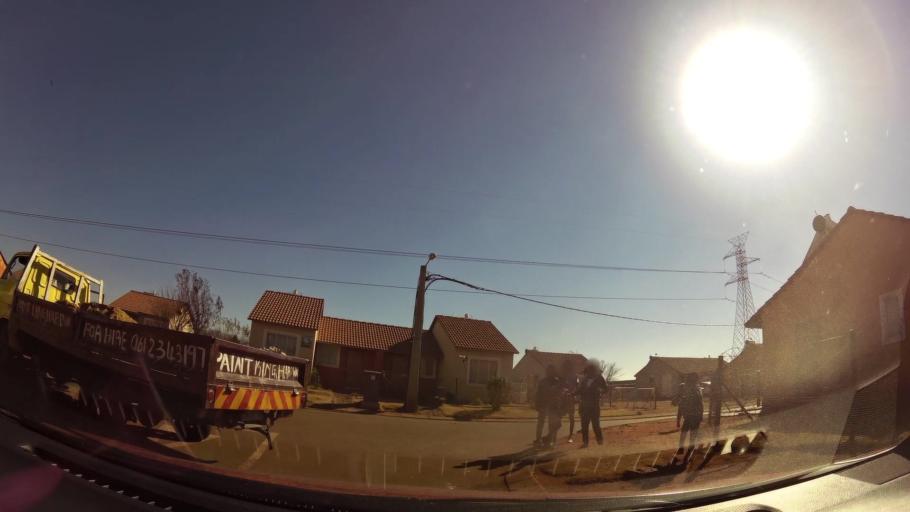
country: ZA
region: Gauteng
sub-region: City of Johannesburg Metropolitan Municipality
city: Soweto
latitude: -26.2342
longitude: 27.7977
